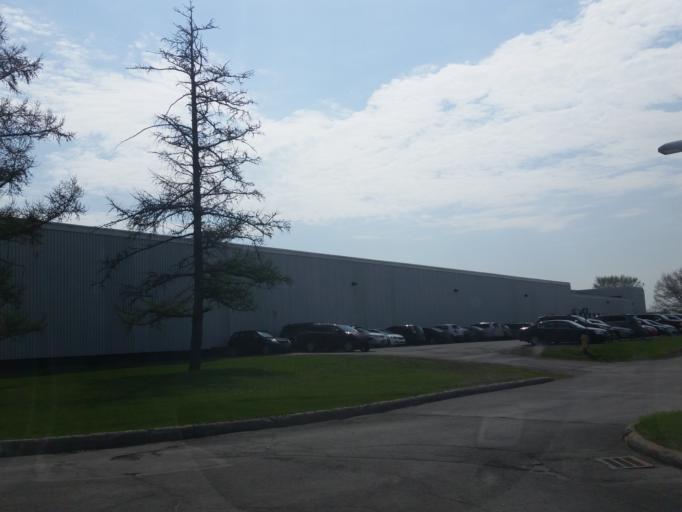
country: CA
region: Quebec
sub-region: Outaouais
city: Gatineau
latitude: 45.4513
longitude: -75.6222
